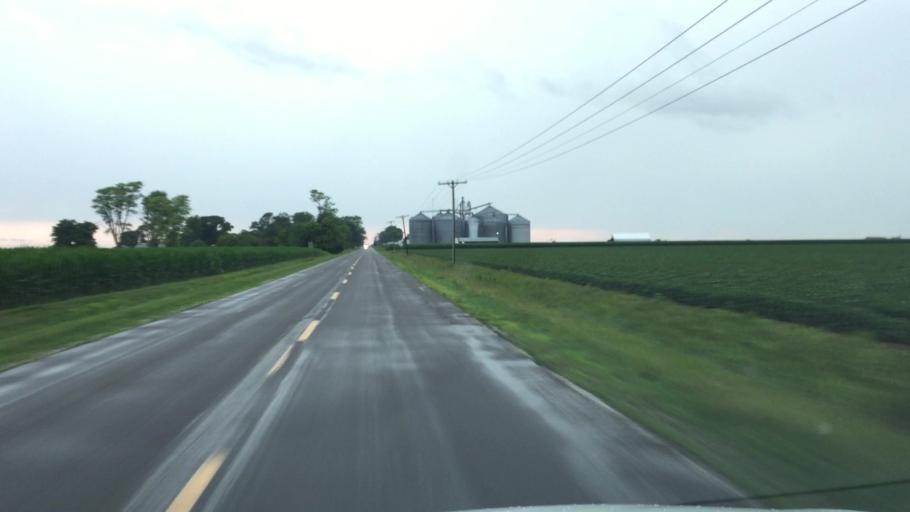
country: US
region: Illinois
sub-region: Hancock County
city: Carthage
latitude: 40.5207
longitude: -91.1590
